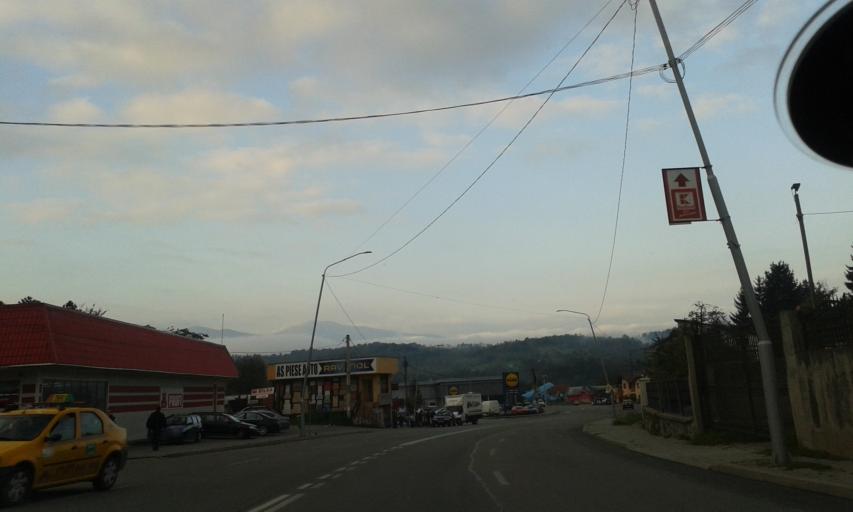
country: RO
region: Hunedoara
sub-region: Municipiul Petrosani
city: Petrosani
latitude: 45.4085
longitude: 23.3748
